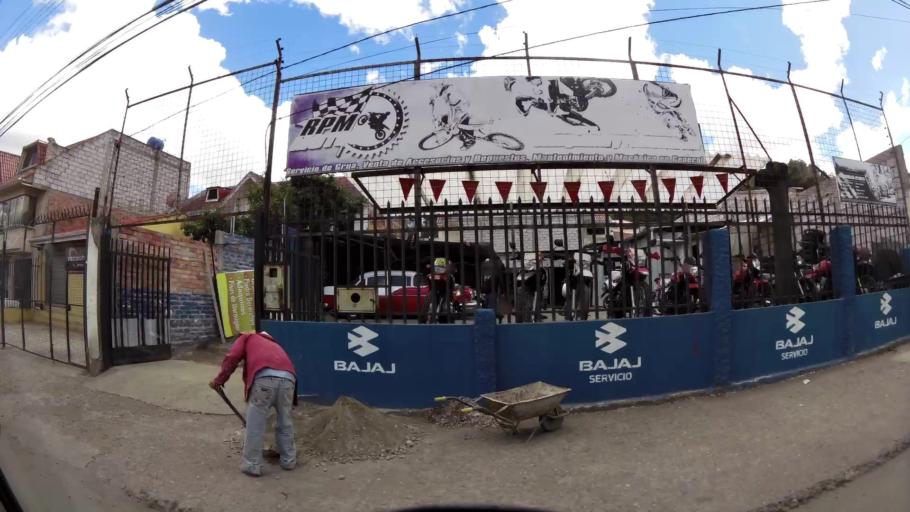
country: EC
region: Azuay
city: Cuenca
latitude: -2.9133
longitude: -78.9881
